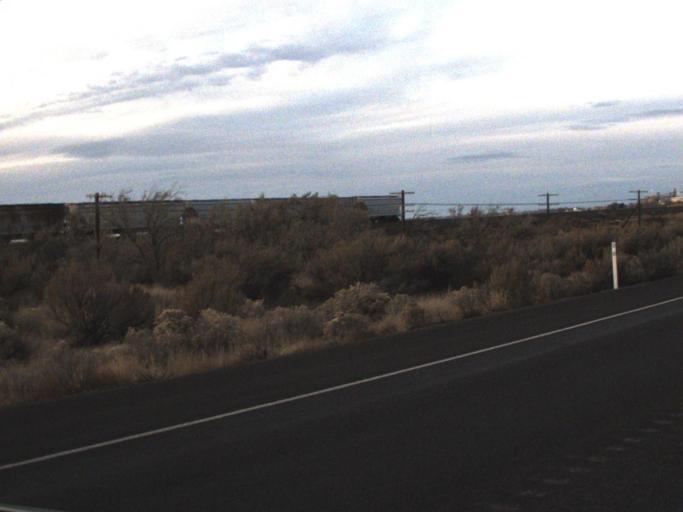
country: US
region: Washington
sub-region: Benton County
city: Finley
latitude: 46.0777
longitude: -118.9077
